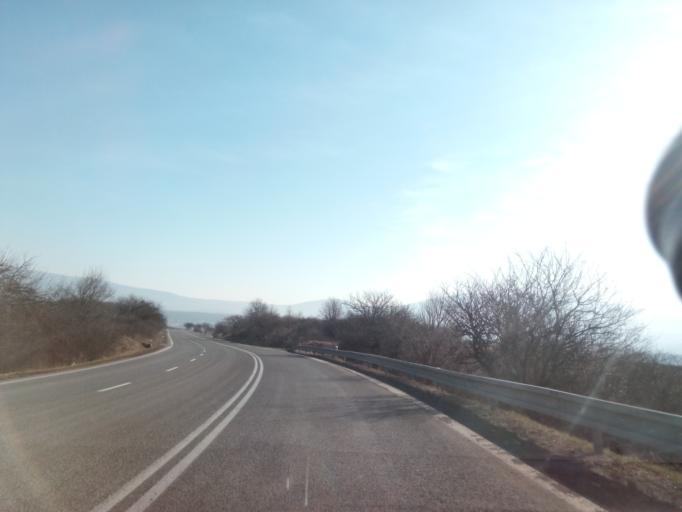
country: SK
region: Kosicky
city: Kosice
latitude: 48.7335
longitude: 21.3973
